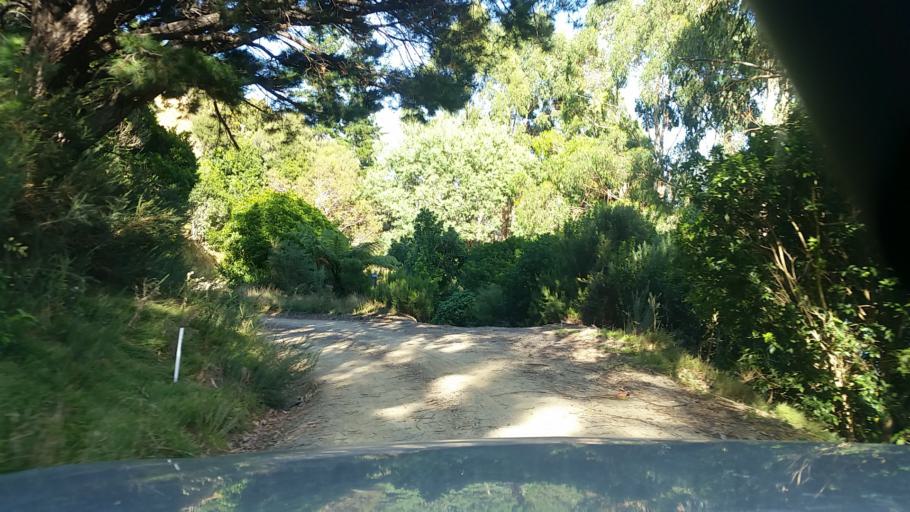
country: NZ
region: Marlborough
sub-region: Marlborough District
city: Picton
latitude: -41.2999
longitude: 174.1794
